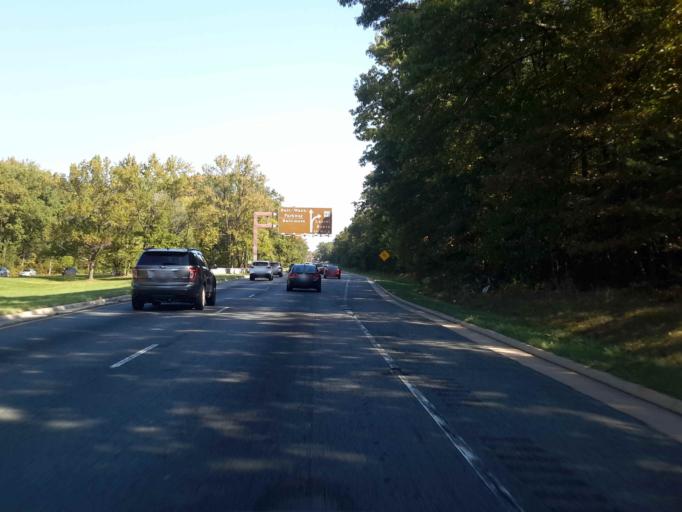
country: US
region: Maryland
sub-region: Prince George's County
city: South Laurel
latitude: 39.0435
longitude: -76.8462
